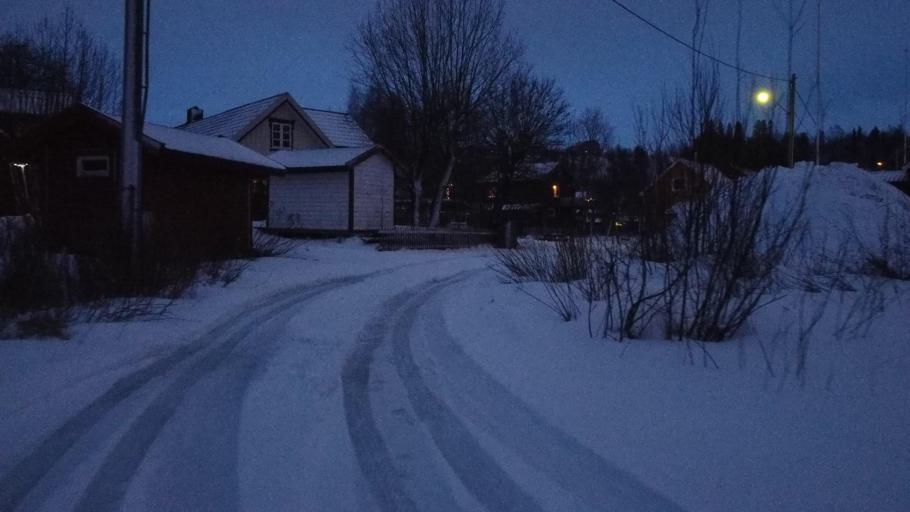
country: NO
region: Nordland
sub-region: Rana
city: Mo i Rana
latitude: 66.3216
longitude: 14.1707
